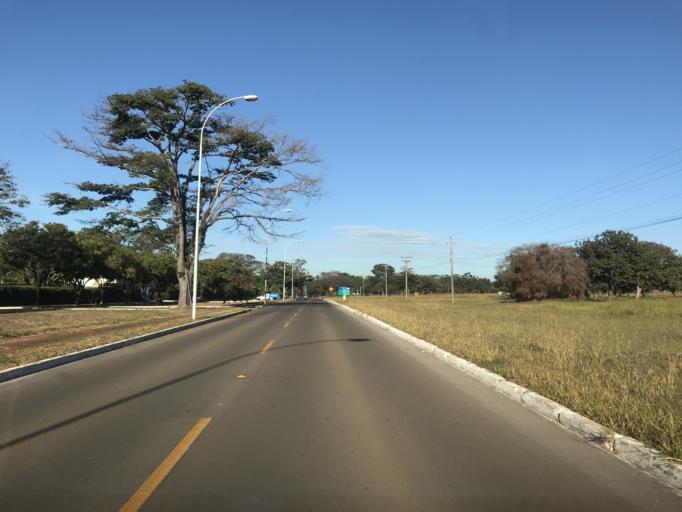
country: BR
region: Federal District
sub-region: Brasilia
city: Brasilia
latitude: -15.8299
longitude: -47.8976
